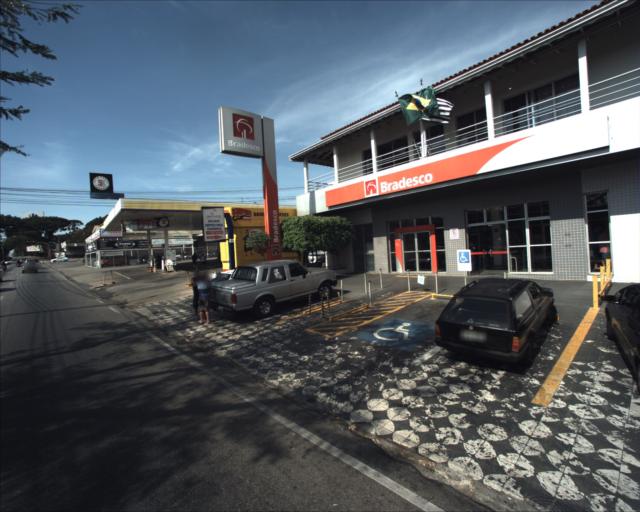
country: BR
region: Sao Paulo
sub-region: Sorocaba
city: Sorocaba
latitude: -23.4839
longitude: -47.4723
